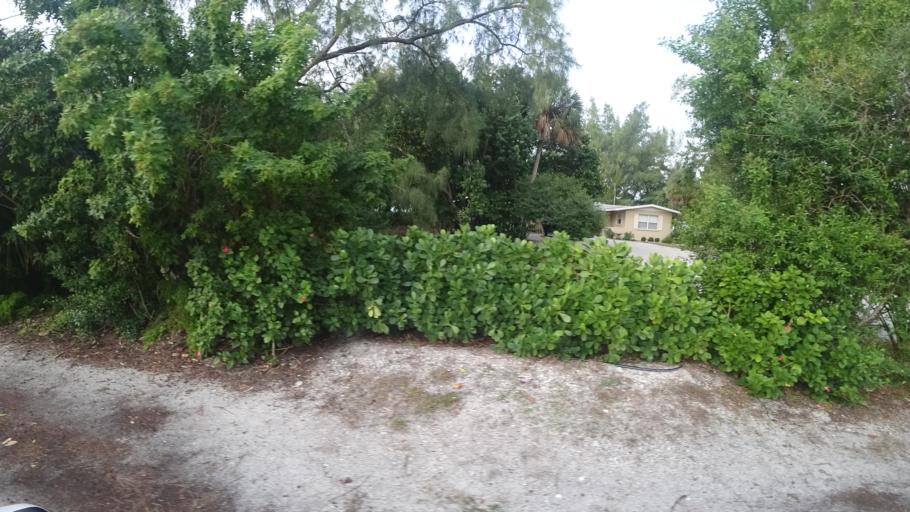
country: US
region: Florida
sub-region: Manatee County
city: Holmes Beach
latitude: 27.5047
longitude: -82.7163
